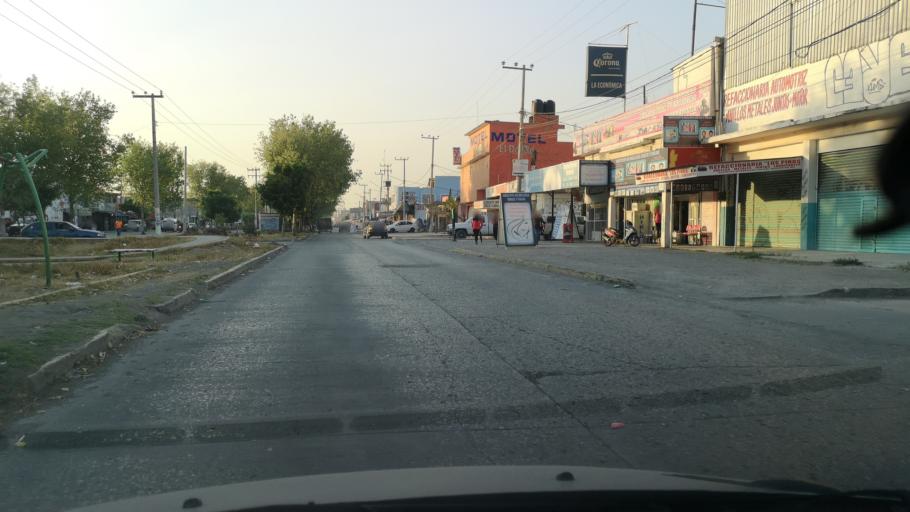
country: MX
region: Mexico
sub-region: Jaltenco
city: Alborada Jaltenco
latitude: 19.6488
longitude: -99.0632
